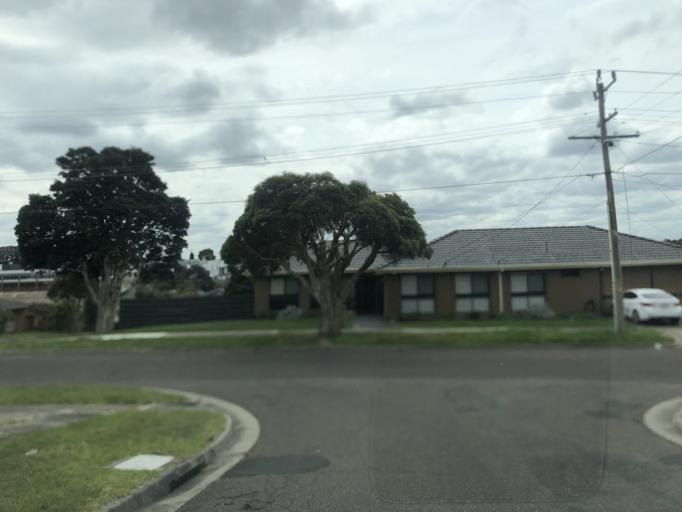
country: AU
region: Victoria
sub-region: Knox
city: Rowville
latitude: -37.9420
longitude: 145.2145
